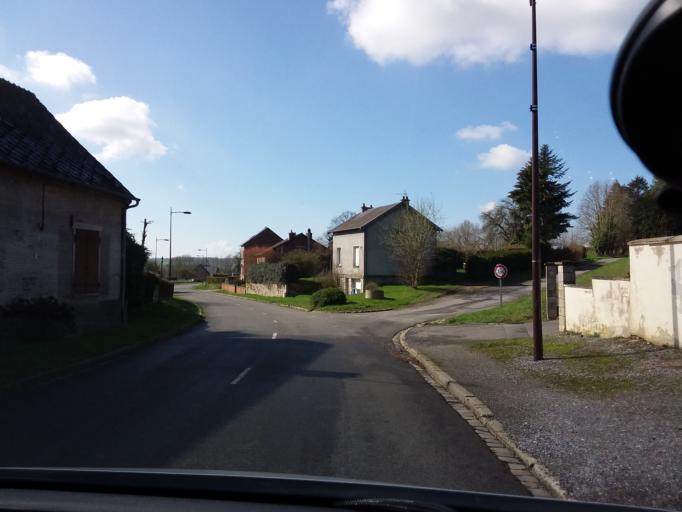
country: FR
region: Picardie
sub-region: Departement de l'Aisne
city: Origny-en-Thierache
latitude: 49.8054
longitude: 4.0129
